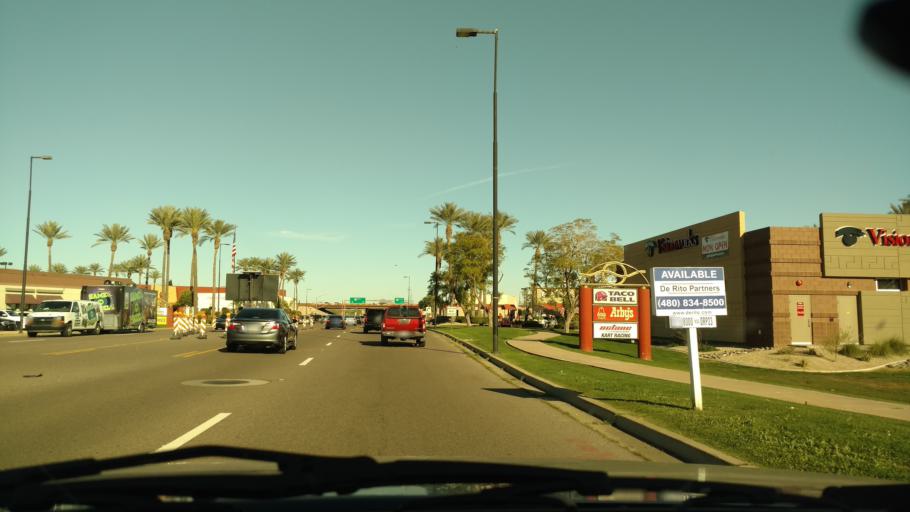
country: US
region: Arizona
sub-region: Maricopa County
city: Scottsdale
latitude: 33.5384
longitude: -111.8858
